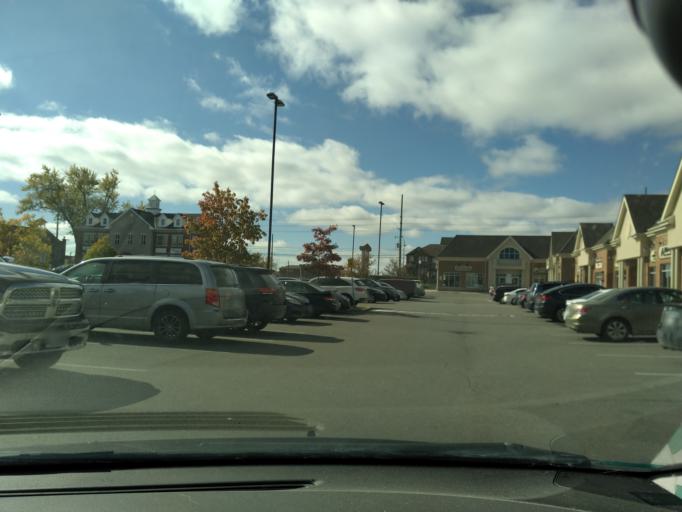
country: CA
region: Ontario
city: Vaughan
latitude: 43.8342
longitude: -79.5566
